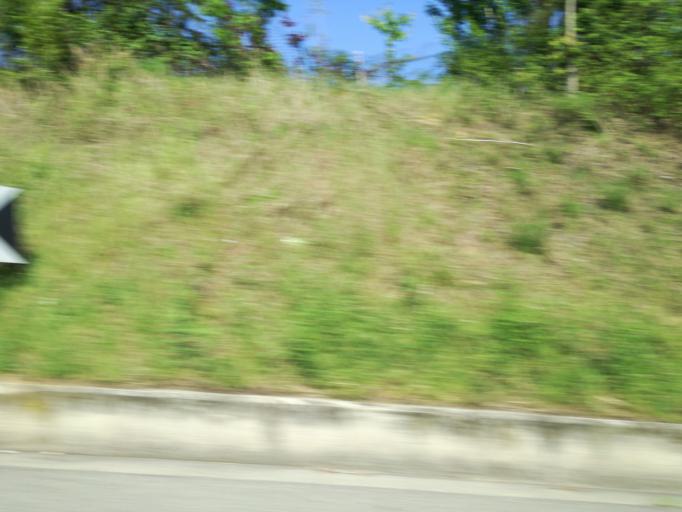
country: IT
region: Lombardy
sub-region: Provincia di Bergamo
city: Bonate Sopra
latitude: 45.6930
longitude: 9.5574
